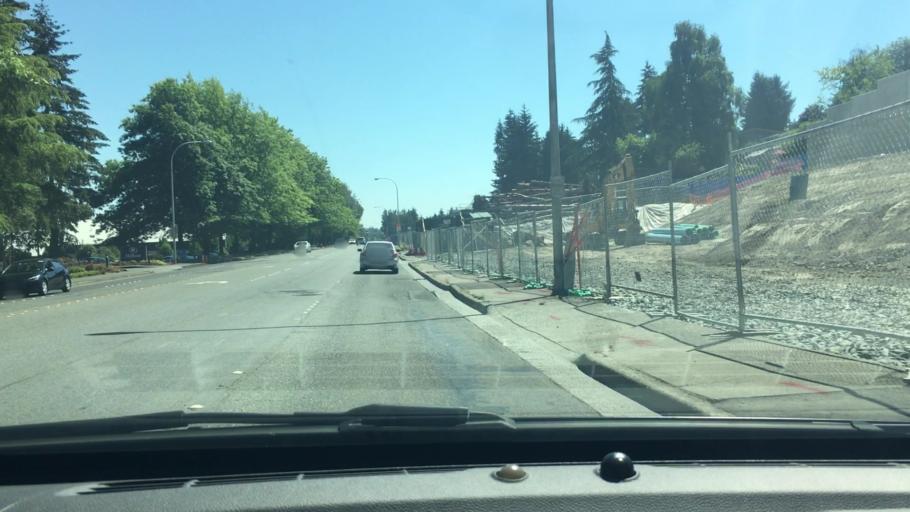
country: US
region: Washington
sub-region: King County
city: Bellevue
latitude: 47.6079
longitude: -122.1909
